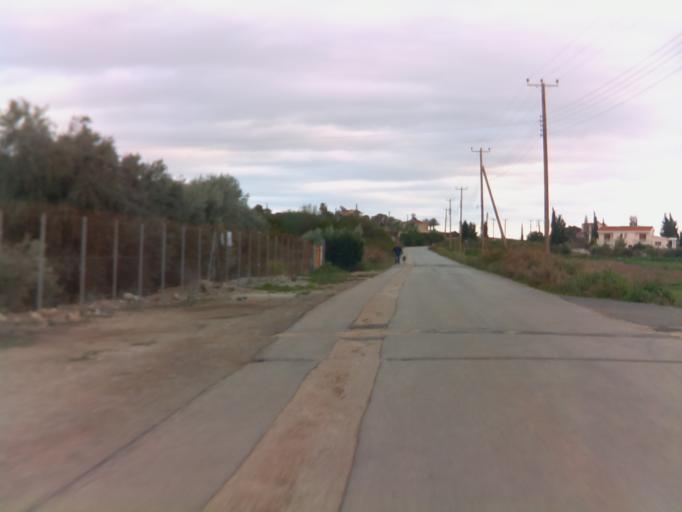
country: CY
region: Pafos
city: Pegeia
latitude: 34.8751
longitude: 32.3441
